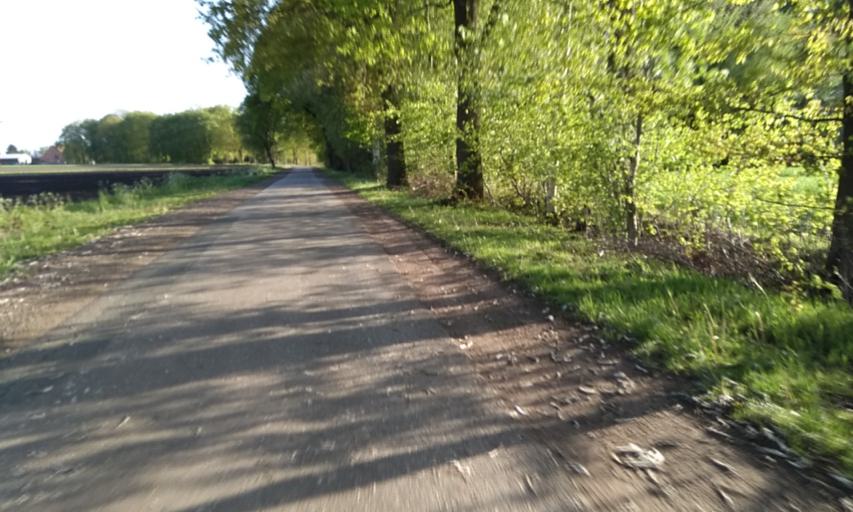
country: DE
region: Lower Saxony
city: Harsefeld
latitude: 53.4218
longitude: 9.5524
